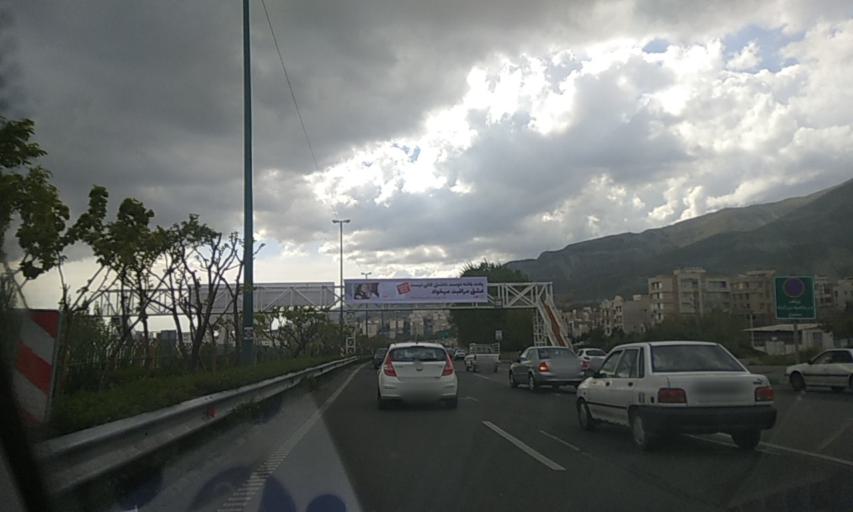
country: IR
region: Tehran
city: Tajrish
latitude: 35.7839
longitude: 51.3568
